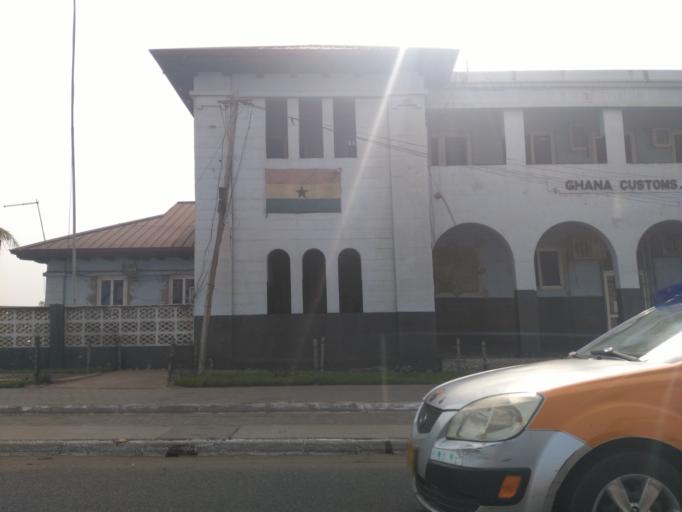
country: GH
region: Greater Accra
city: Accra
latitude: 5.5352
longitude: -0.2110
